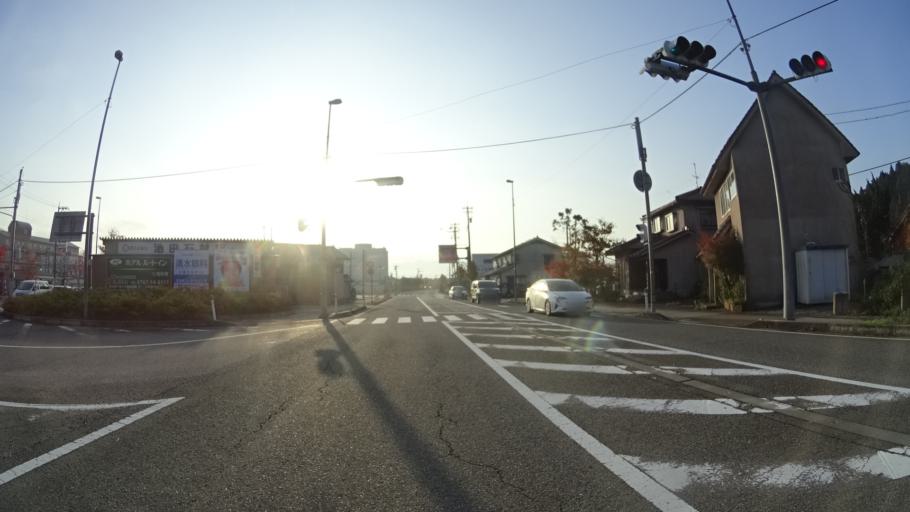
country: JP
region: Ishikawa
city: Nanao
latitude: 37.0564
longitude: 136.9531
